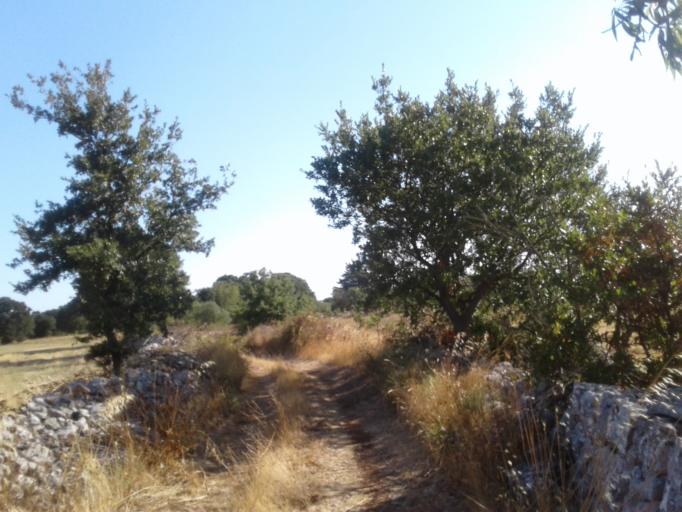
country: IT
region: Apulia
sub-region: Provincia di Bari
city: Gioia del Colle
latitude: 40.8222
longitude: 16.9497
